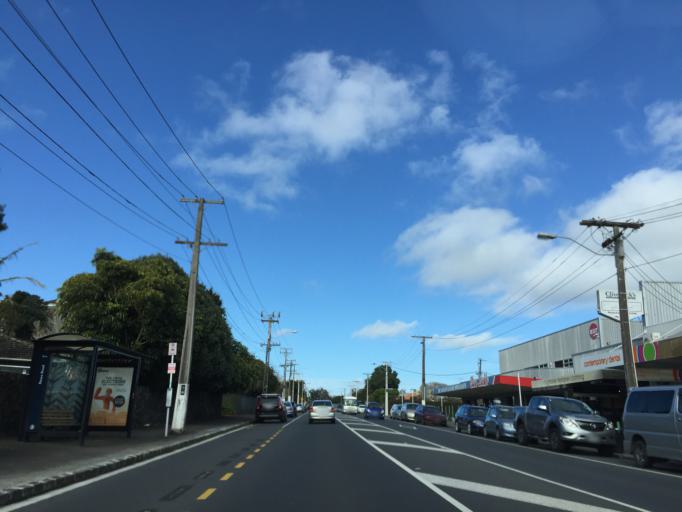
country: NZ
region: Auckland
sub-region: Auckland
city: Auckland
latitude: -36.8997
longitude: 174.7570
